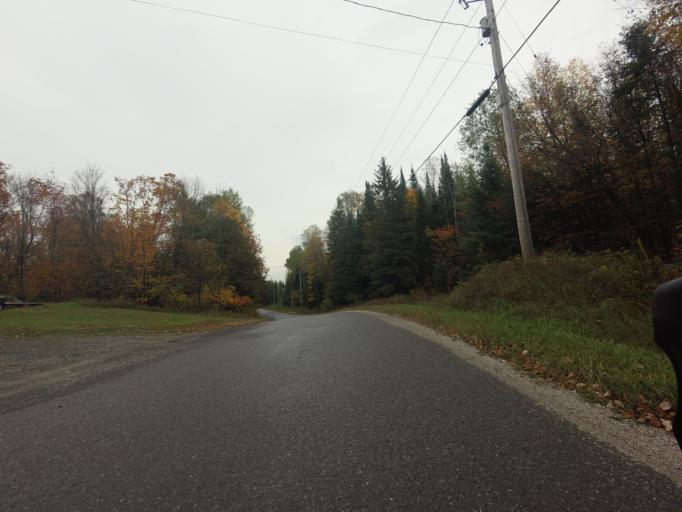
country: CA
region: Ontario
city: Perth
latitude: 45.1151
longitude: -76.5086
